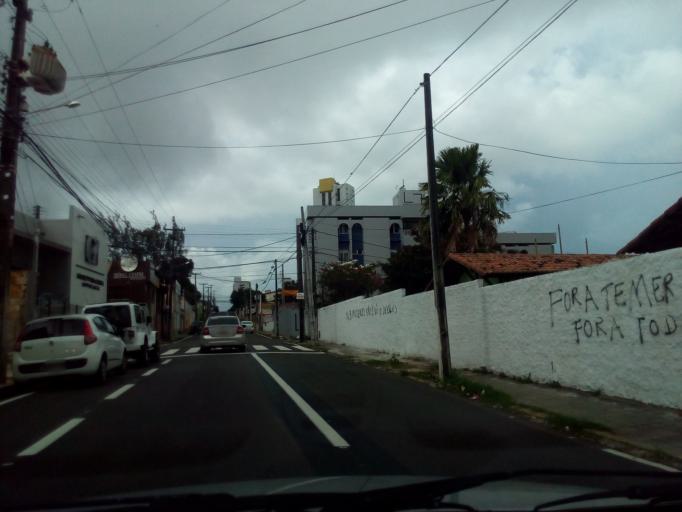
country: BR
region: Rio Grande do Norte
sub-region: Natal
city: Natal
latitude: -5.7999
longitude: -35.2085
